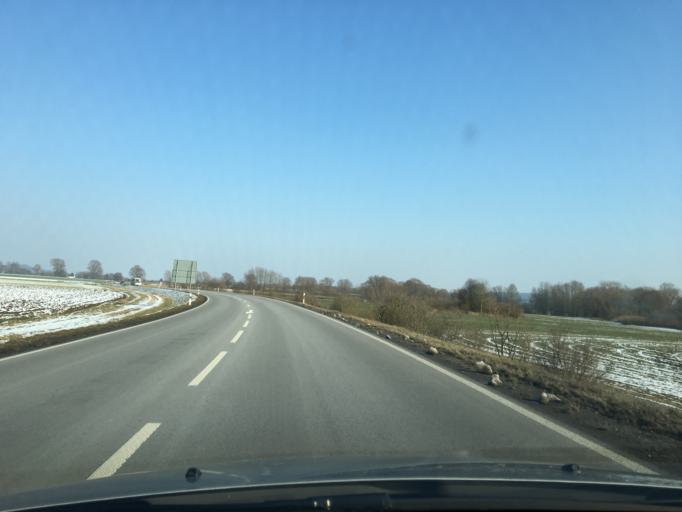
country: DE
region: Bavaria
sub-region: Lower Bavaria
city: Frontenhausen
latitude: 48.5538
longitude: 12.5291
